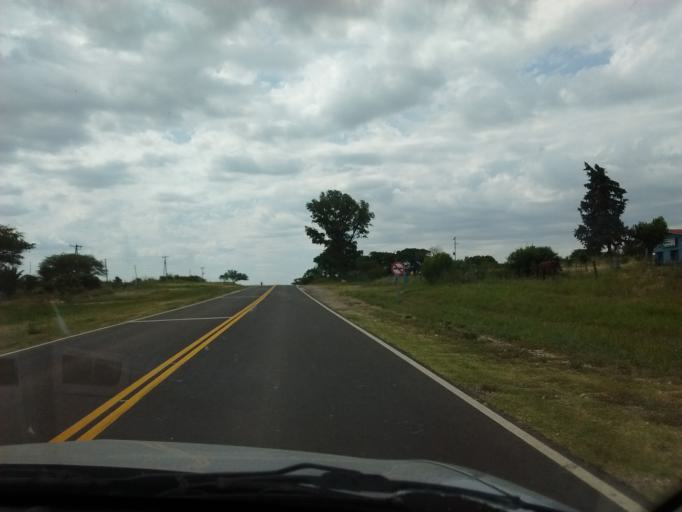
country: AR
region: Entre Rios
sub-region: Departamento de Victoria
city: Victoria
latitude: -32.8342
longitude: -59.8703
